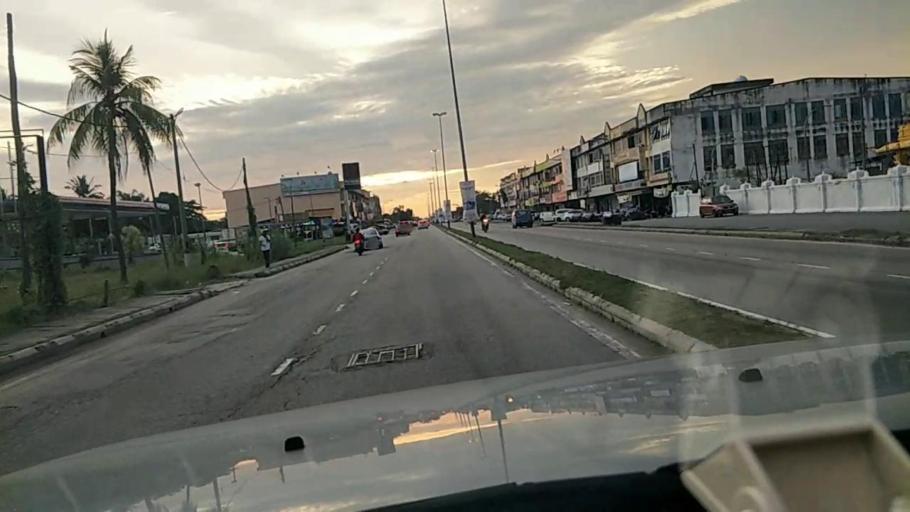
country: MY
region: Perak
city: Kampong Dungun
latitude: 3.1388
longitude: 101.3696
